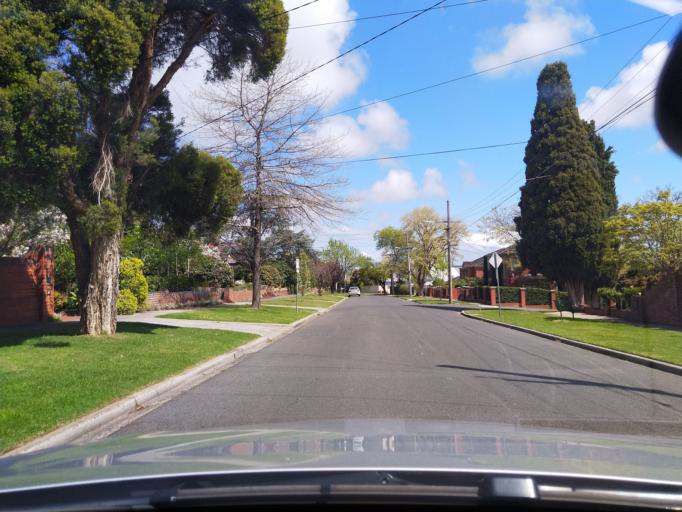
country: AU
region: Victoria
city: Rosanna
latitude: -37.7618
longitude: 145.0580
